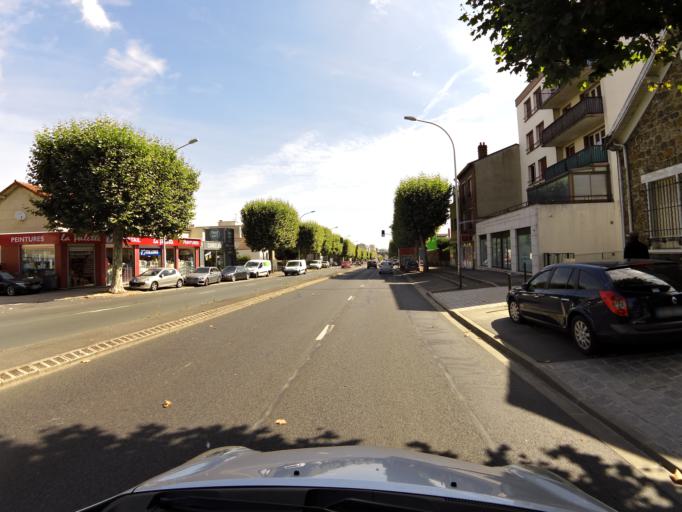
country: FR
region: Ile-de-France
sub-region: Departement du Val-de-Marne
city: Le Perreux-sur-Marne
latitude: 48.8511
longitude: 2.5050
